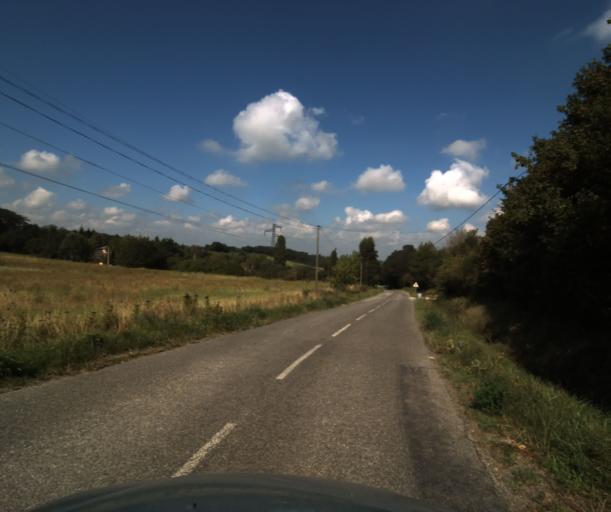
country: FR
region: Midi-Pyrenees
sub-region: Departement de la Haute-Garonne
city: Vieille-Toulouse
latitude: 43.5095
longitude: 1.4363
